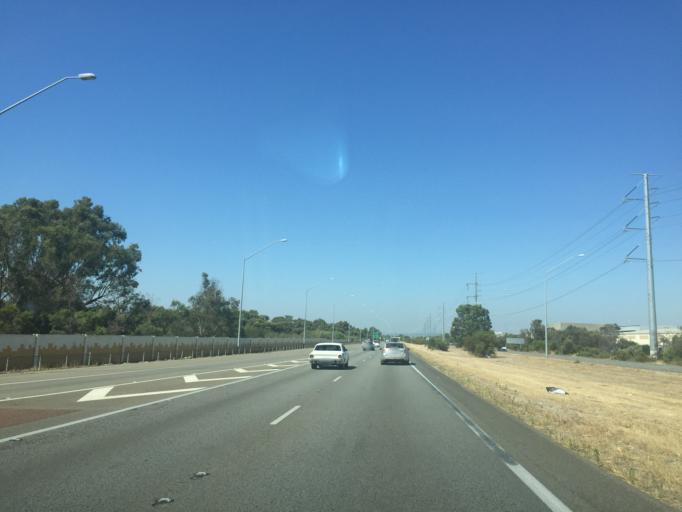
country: AU
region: Western Australia
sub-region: Canning
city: Willetton
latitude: -32.0656
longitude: 115.8939
